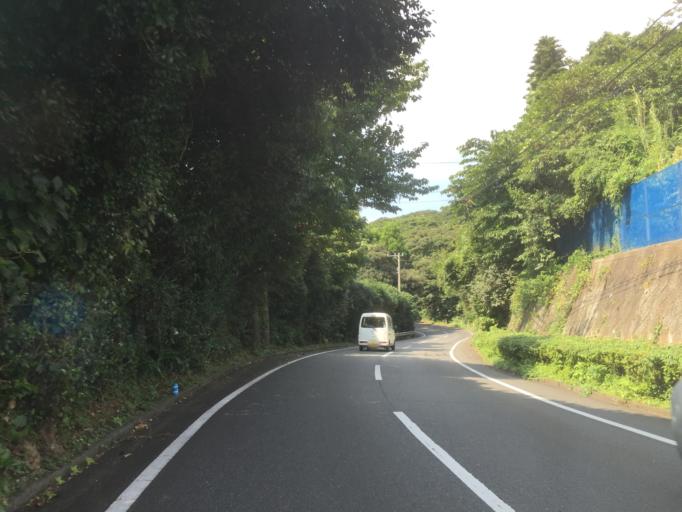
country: JP
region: Shizuoka
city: Shimoda
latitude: 34.0555
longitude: 139.5336
